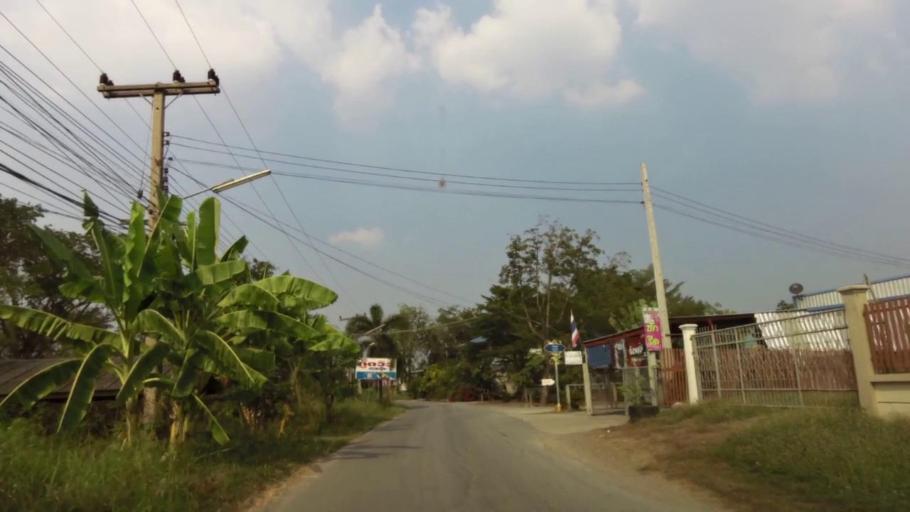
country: TH
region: Phra Nakhon Si Ayutthaya
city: Phra Nakhon Si Ayutthaya
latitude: 14.3062
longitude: 100.5644
